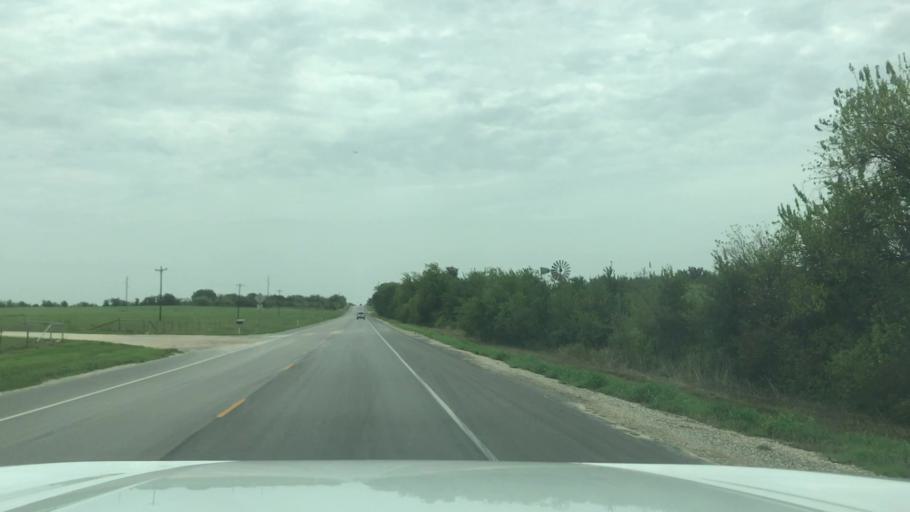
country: US
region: Texas
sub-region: Erath County
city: Dublin
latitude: 32.0903
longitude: -98.2630
